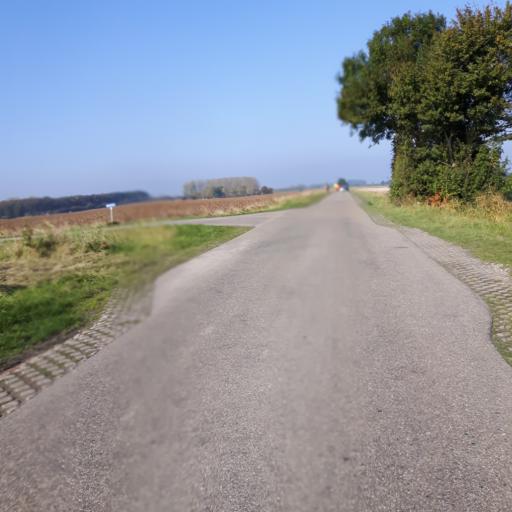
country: NL
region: Zeeland
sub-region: Gemeente Reimerswaal
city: Yerseke
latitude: 51.4763
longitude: 3.9867
